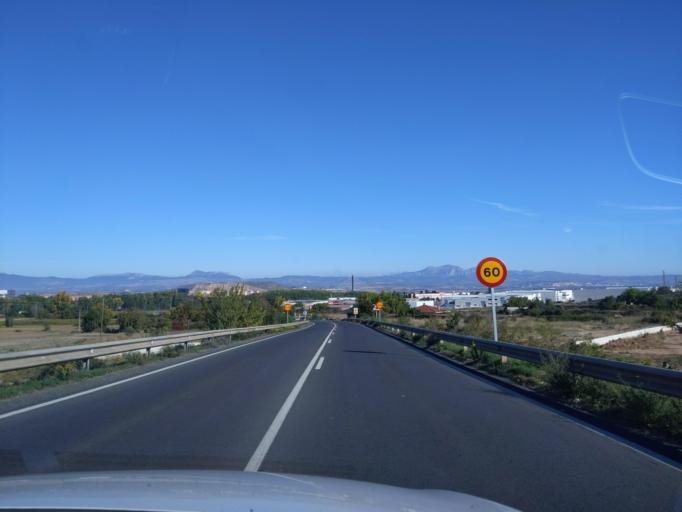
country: ES
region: La Rioja
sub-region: Provincia de La Rioja
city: Villamediana de Iregua
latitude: 42.4420
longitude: -2.4189
